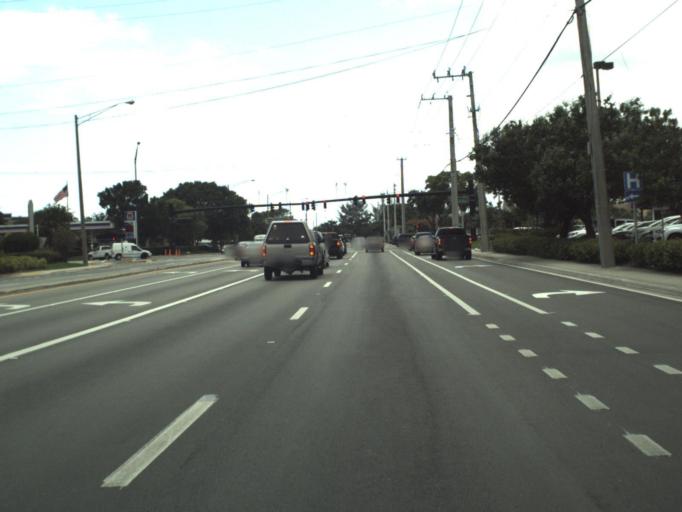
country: US
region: Florida
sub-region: Broward County
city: North Andrews Gardens
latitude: 26.1900
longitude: -80.1334
